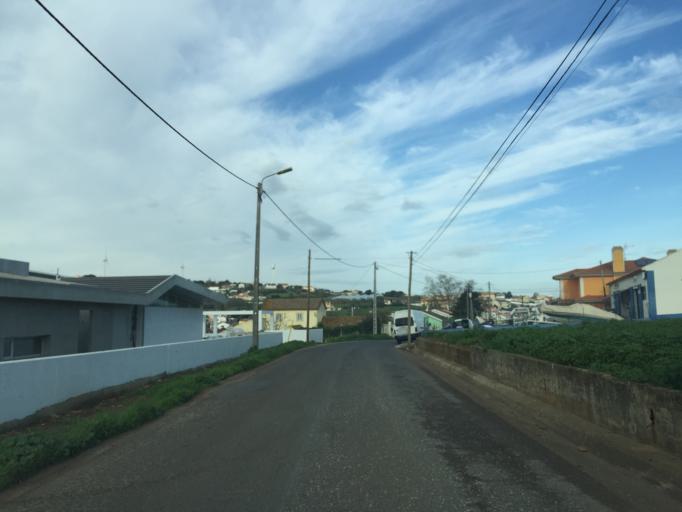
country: PT
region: Lisbon
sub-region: Sintra
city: Almargem
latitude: 38.8316
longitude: -9.2503
